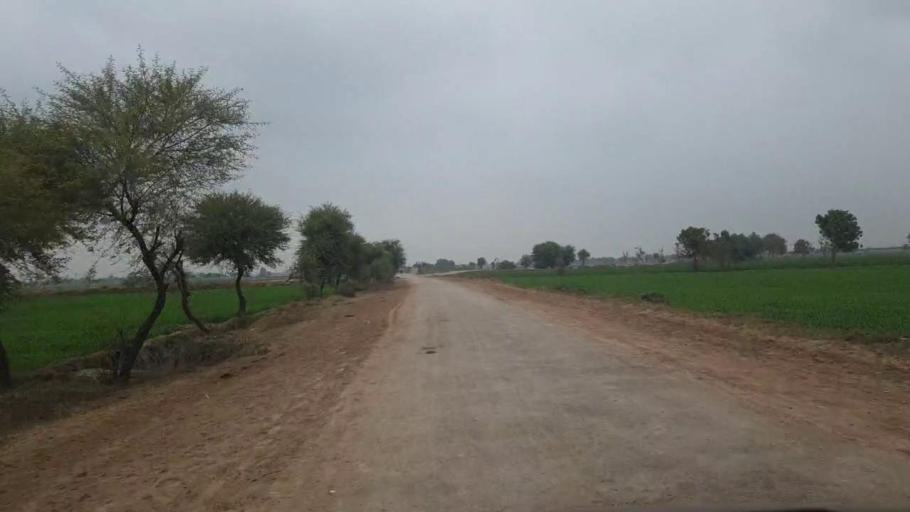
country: PK
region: Sindh
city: Shahdadpur
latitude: 25.9544
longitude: 68.7239
